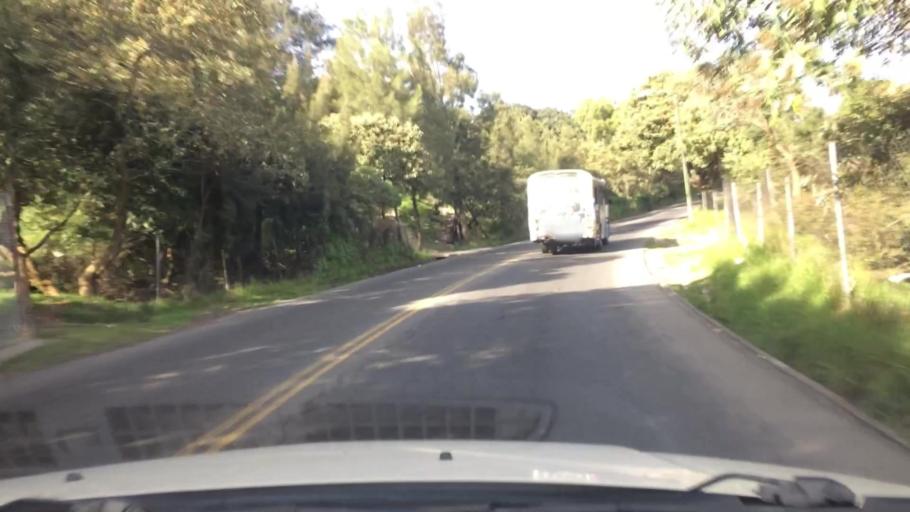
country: MX
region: Mexico City
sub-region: Tlalpan
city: Lomas de Tepemecatl
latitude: 19.2662
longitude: -99.2256
